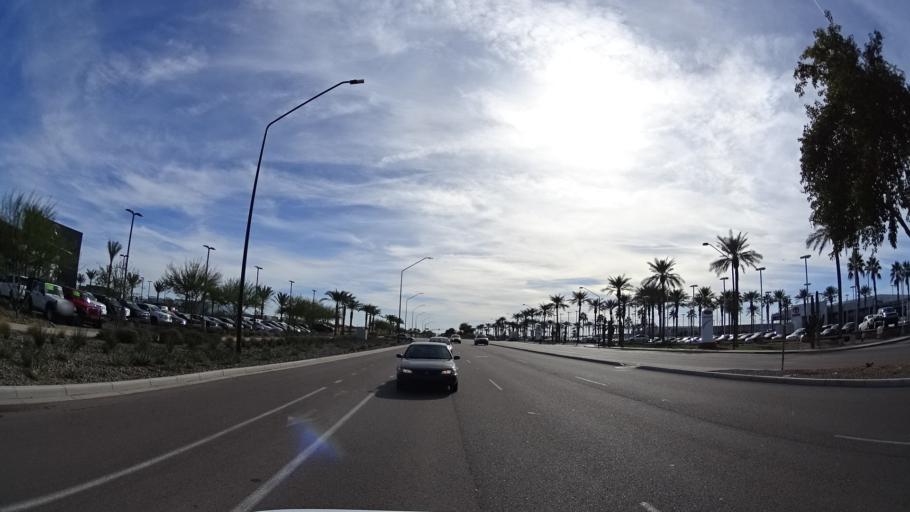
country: US
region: Arizona
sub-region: Maricopa County
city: Chandler
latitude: 33.2886
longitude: -111.7896
